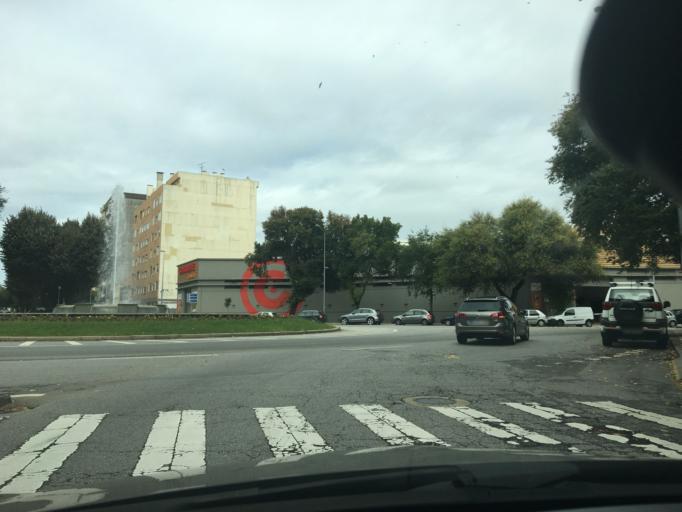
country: PT
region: Porto
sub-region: Matosinhos
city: Matosinhos
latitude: 41.1786
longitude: -8.6813
